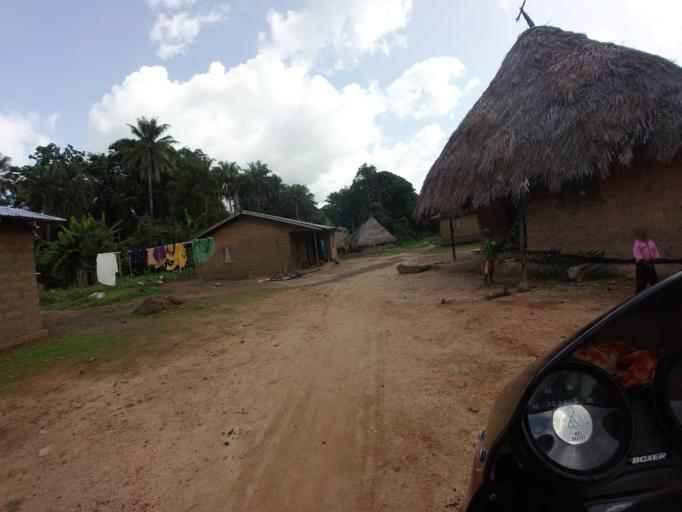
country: SL
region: Eastern Province
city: Tombu
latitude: 8.5399
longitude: -10.7312
